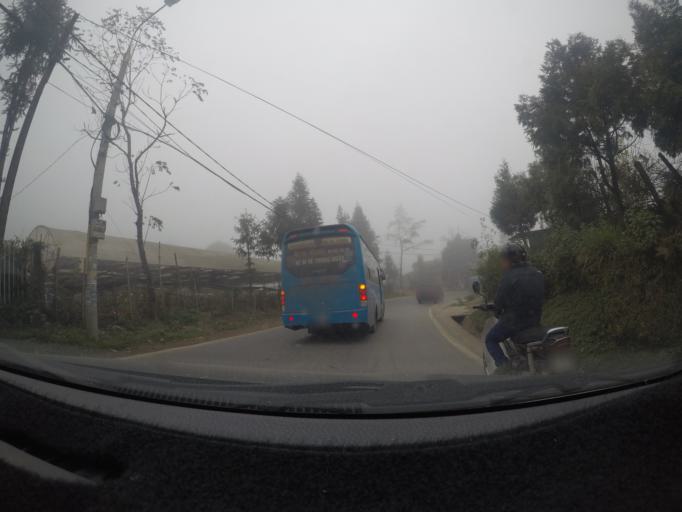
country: VN
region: Lao Cai
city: Sa Pa
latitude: 22.3441
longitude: 103.8561
